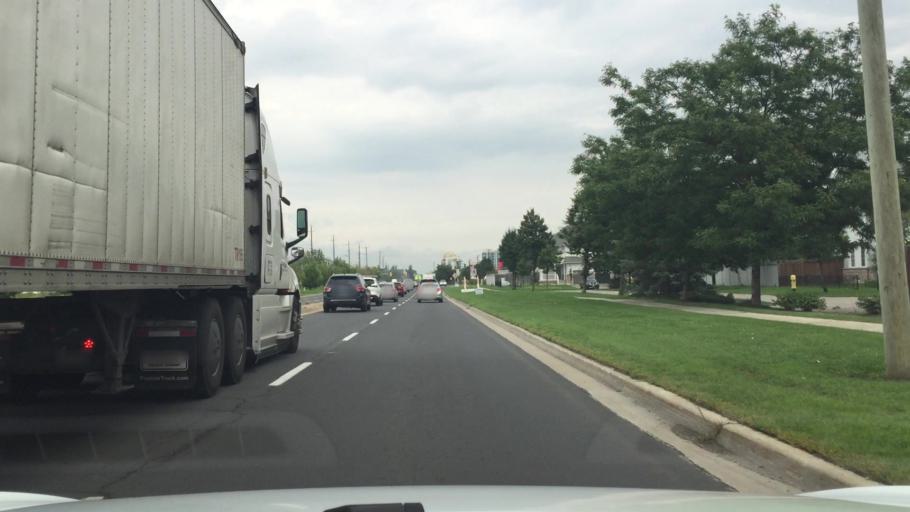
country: CA
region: Ontario
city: Ajax
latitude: 43.8590
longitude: -78.9492
